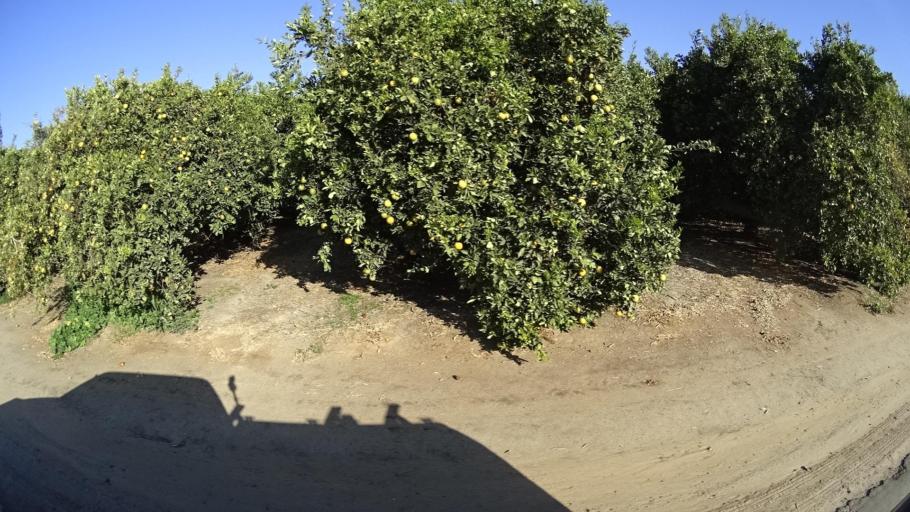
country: US
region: California
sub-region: Tulare County
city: Richgrove
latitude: 35.7326
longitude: -119.1355
